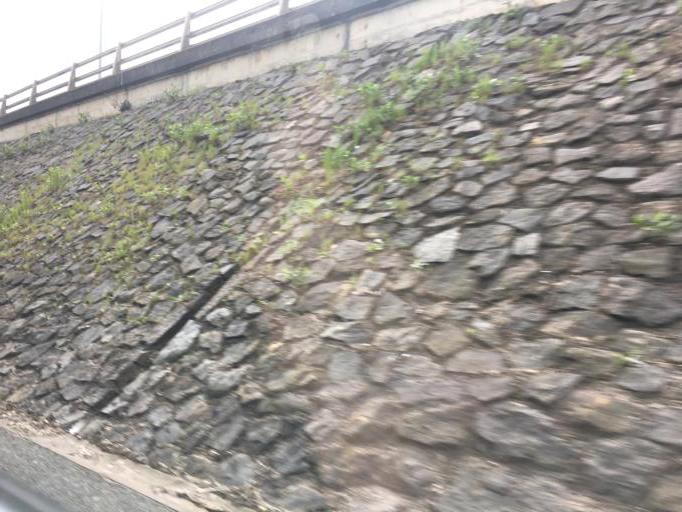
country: GB
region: Wales
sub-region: Gwynedd
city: Caernarfon
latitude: 53.1407
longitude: -4.2710
